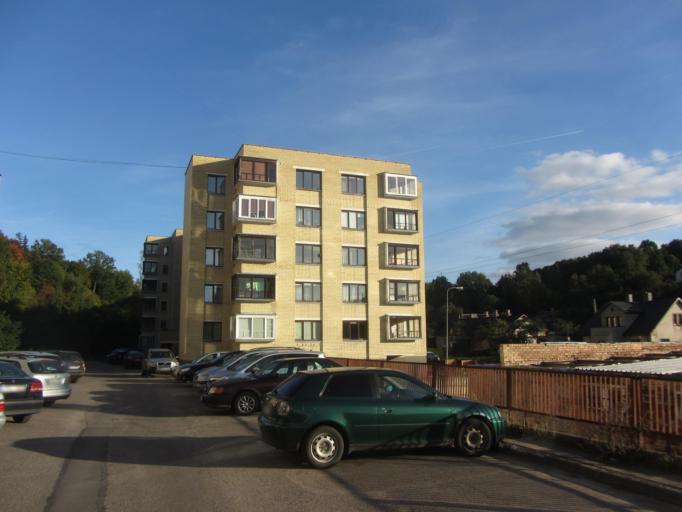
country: LT
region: Vilnius County
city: Lazdynai
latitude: 54.6414
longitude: 25.2090
